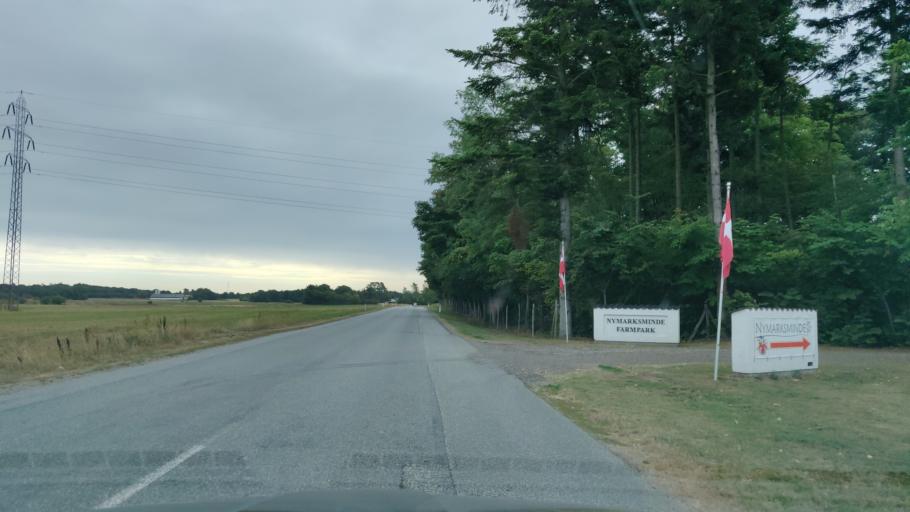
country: DK
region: North Denmark
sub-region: Alborg Kommune
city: Vodskov
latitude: 57.1125
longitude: 10.0622
